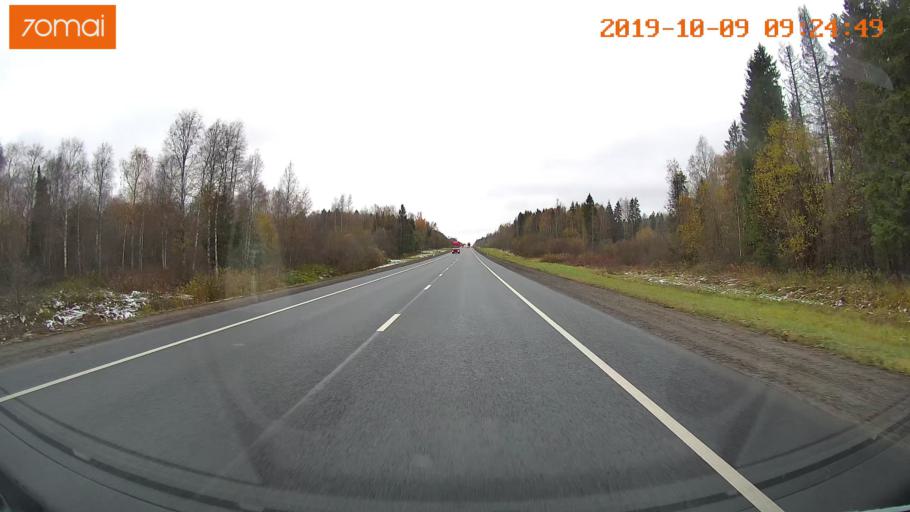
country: RU
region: Vologda
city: Vologda
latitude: 59.0833
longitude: 40.0108
